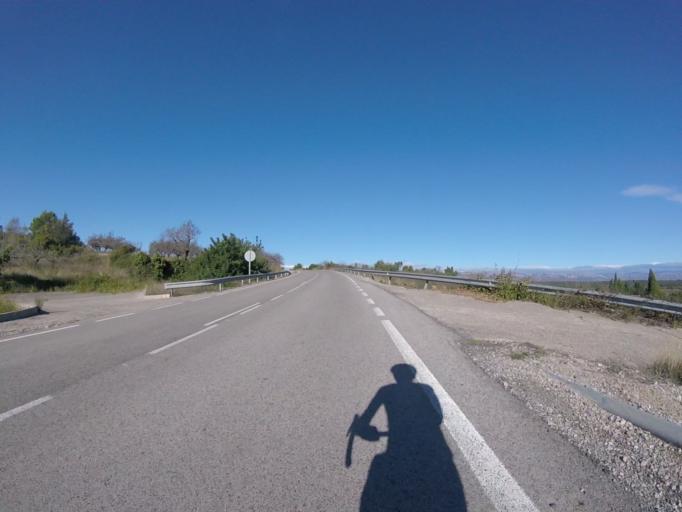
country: ES
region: Valencia
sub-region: Provincia de Castello
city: Cervera del Maestre
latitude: 40.4721
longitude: 0.2400
